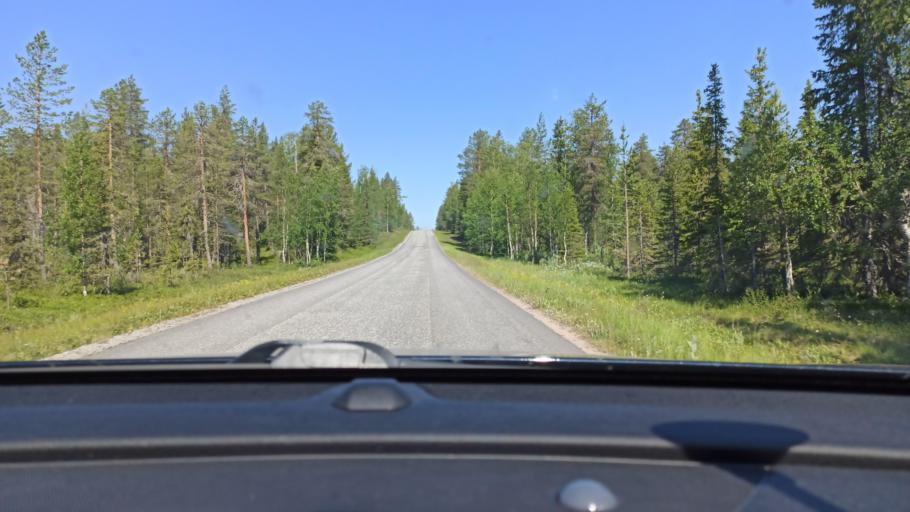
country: FI
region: Lapland
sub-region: Tunturi-Lappi
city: Kolari
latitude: 67.6781
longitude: 24.1413
